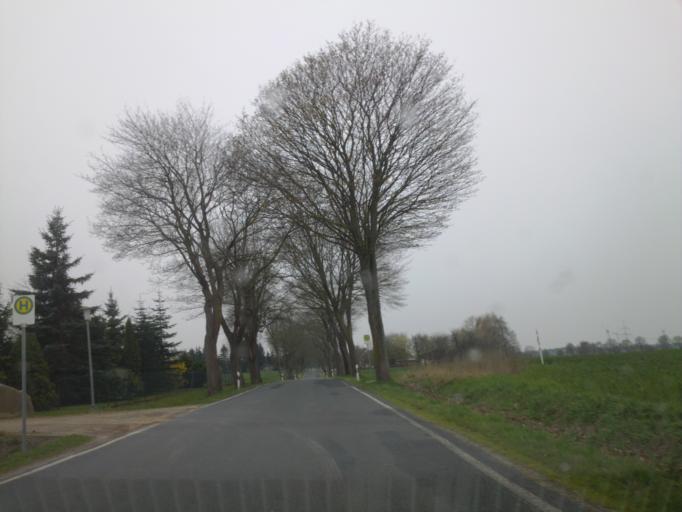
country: DE
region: Mecklenburg-Vorpommern
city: Bad Sulze
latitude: 54.1588
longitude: 12.7162
